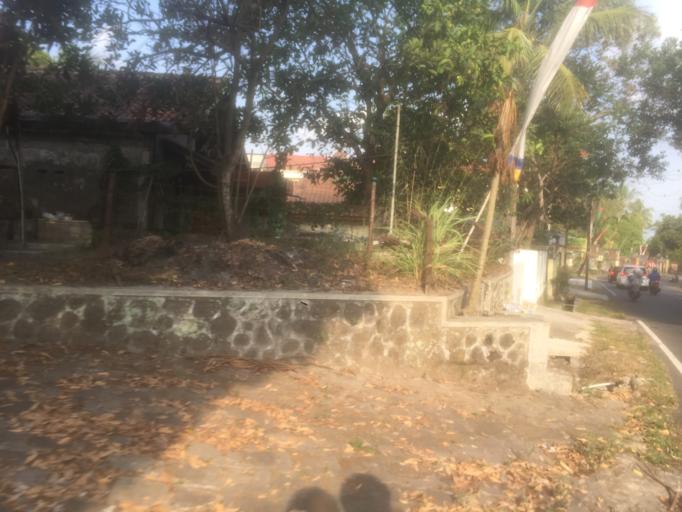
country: ID
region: Daerah Istimewa Yogyakarta
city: Sleman
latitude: -7.6547
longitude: 110.4230
